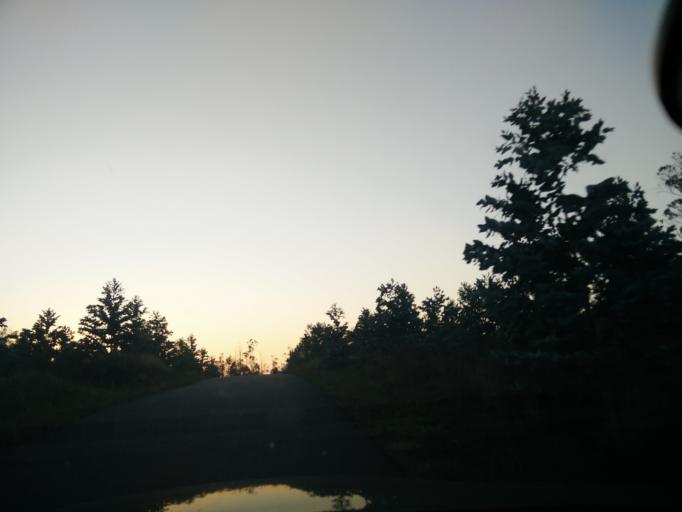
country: ES
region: Galicia
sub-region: Provincia da Coruna
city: Monfero
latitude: 43.3495
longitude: -8.0426
